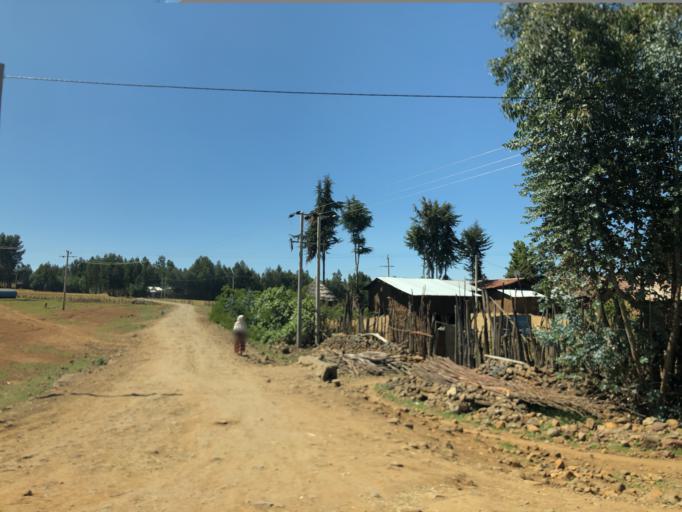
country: ET
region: Amhara
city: Lalibela
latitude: 11.7356
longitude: 38.7552
